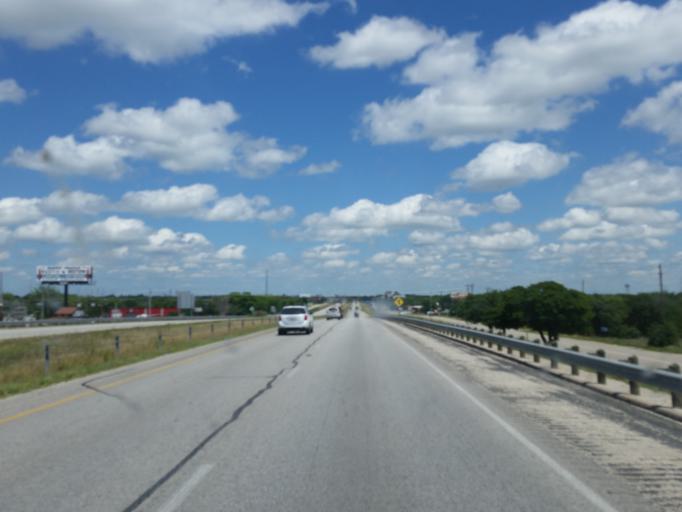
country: US
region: Texas
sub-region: Callahan County
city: Clyde
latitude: 32.4150
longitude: -99.5077
